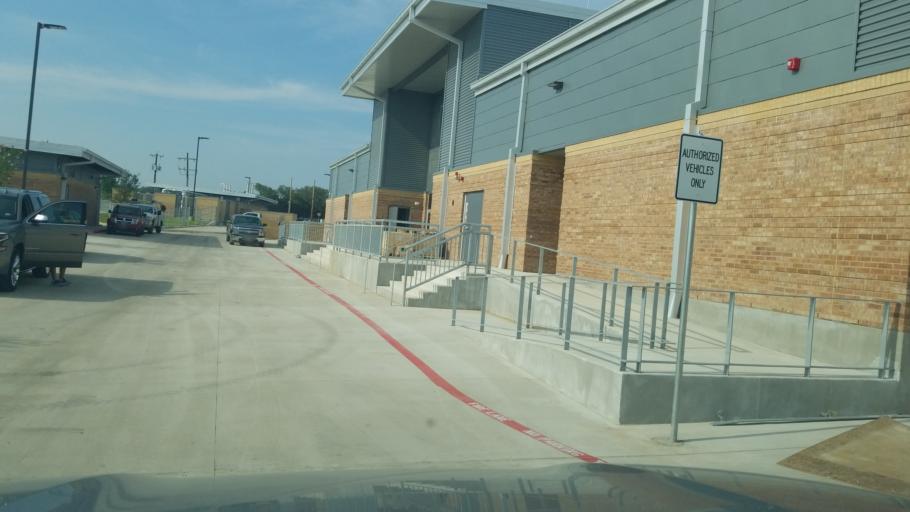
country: US
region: Texas
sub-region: Bexar County
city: Timberwood Park
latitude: 29.7178
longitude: -98.4695
